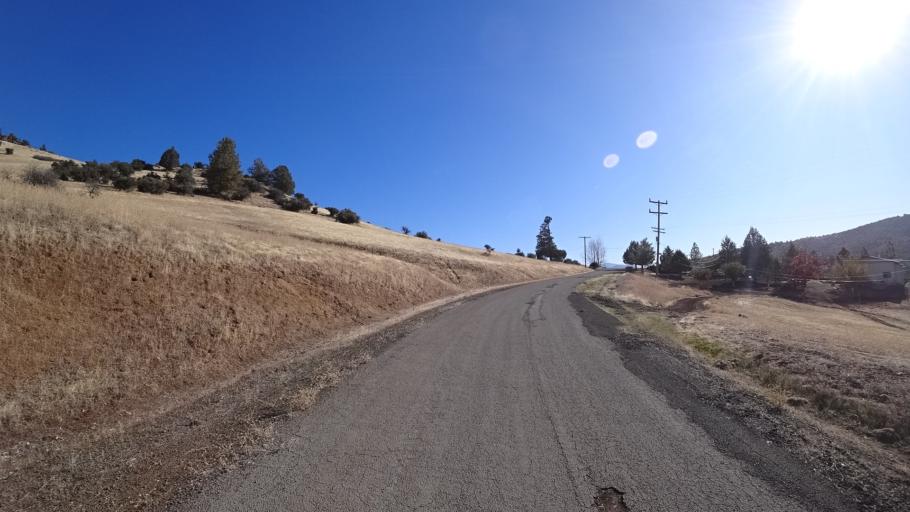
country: US
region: California
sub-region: Siskiyou County
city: Montague
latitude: 41.8996
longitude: -122.5222
